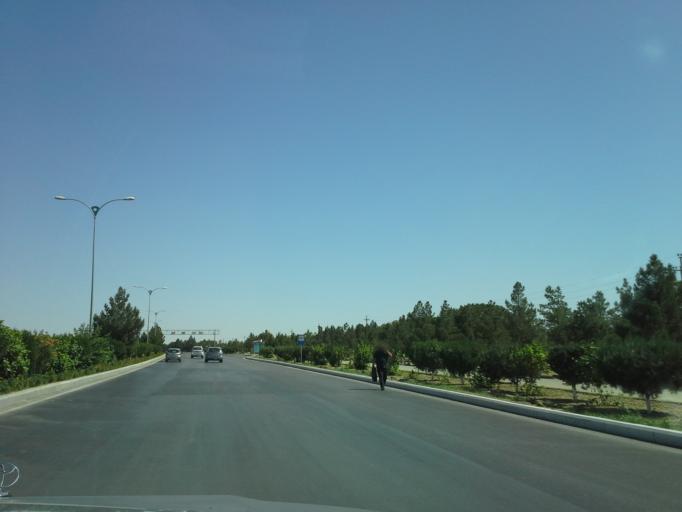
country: TM
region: Ahal
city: Annau
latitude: 37.9196
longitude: 58.4505
